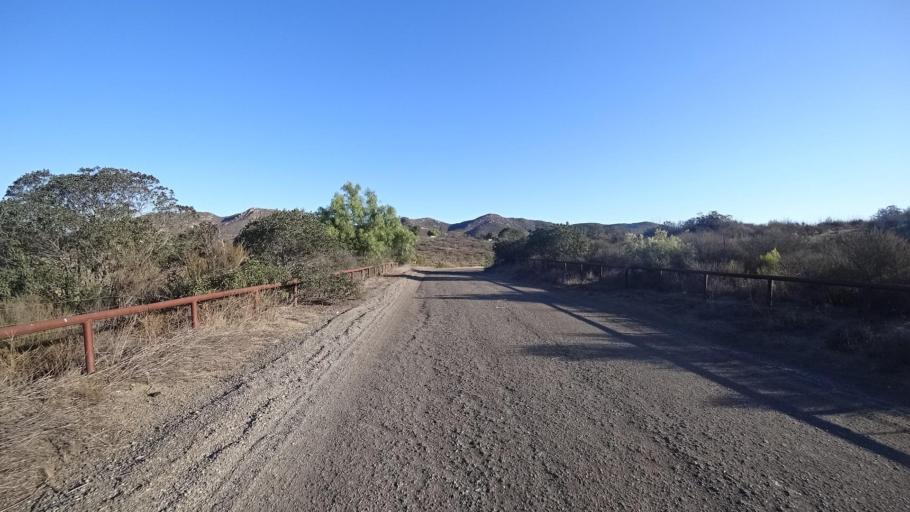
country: US
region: California
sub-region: San Diego County
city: Jamul
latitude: 32.7005
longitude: -116.9044
